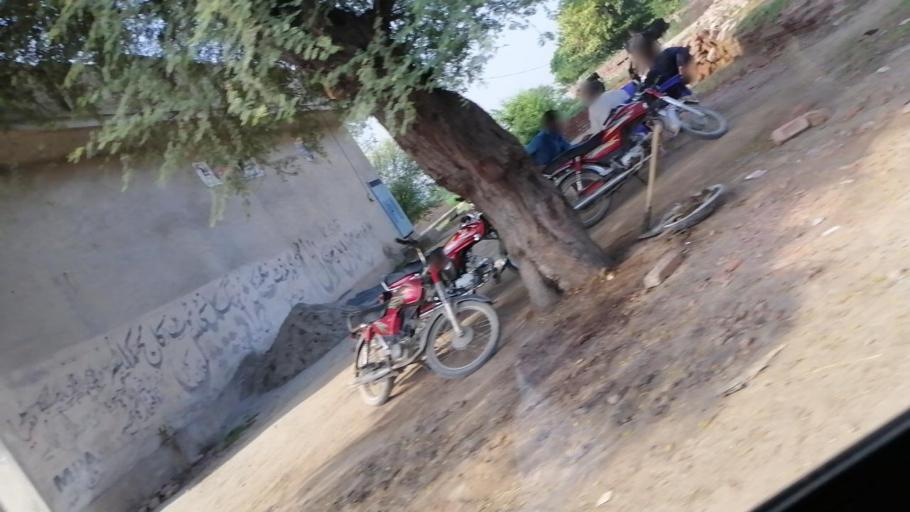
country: PK
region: Punjab
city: Kamalia
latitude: 30.7178
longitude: 72.6748
